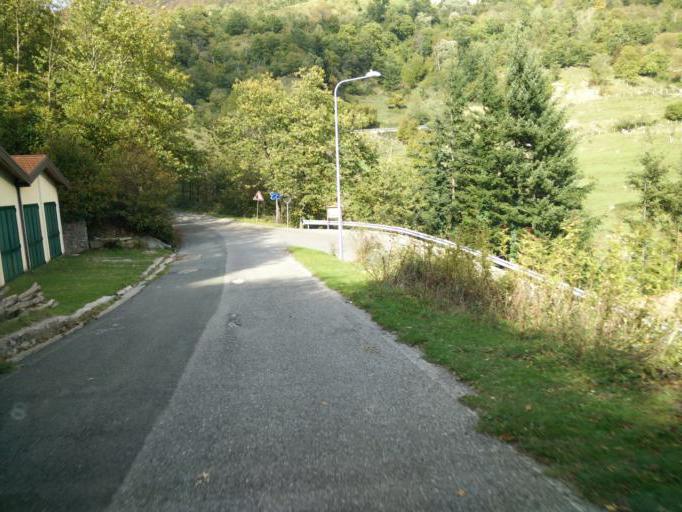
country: IT
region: Tuscany
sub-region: Provincia di Massa-Carrara
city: Patigno
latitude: 44.3516
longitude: 9.7146
